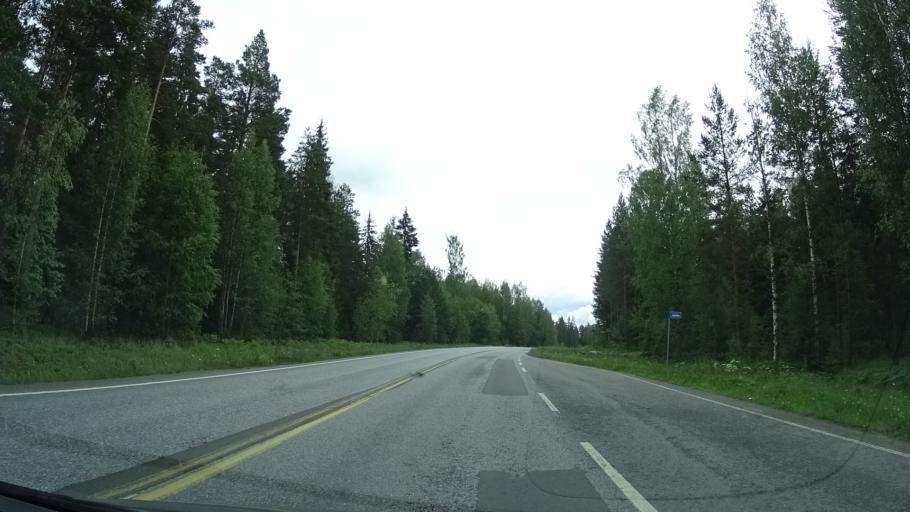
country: FI
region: Pirkanmaa
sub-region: Etelae-Pirkanmaa
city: Urjala
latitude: 61.0865
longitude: 23.5196
